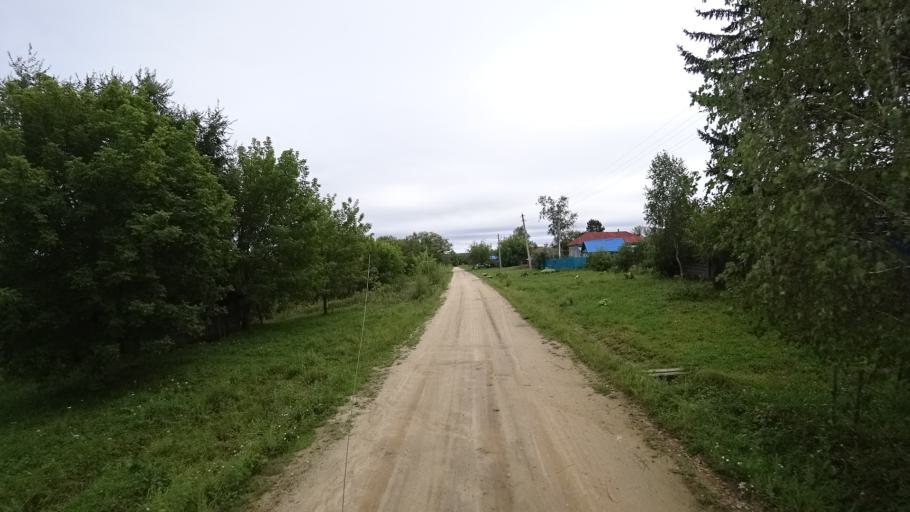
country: RU
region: Primorskiy
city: Rettikhovka
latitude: 44.1368
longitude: 132.6431
